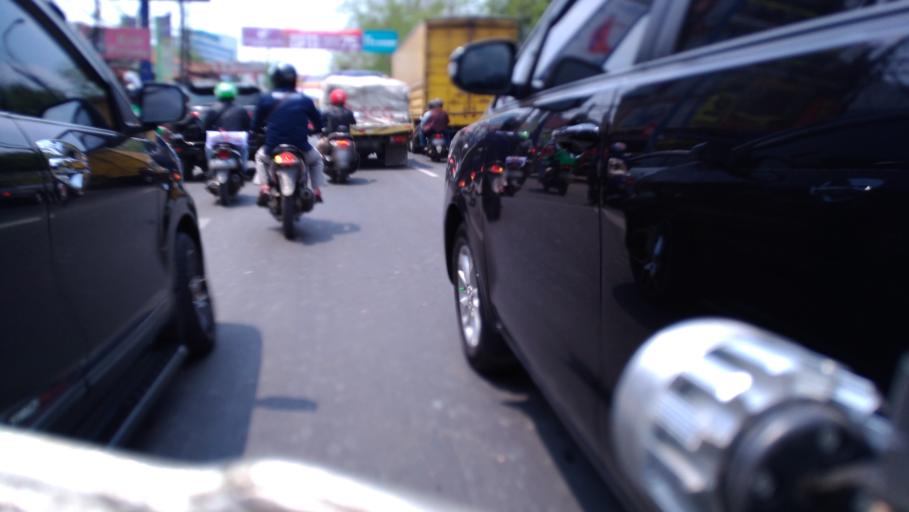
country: ID
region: West Java
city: Cileungsir
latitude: -6.3754
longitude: 106.9137
